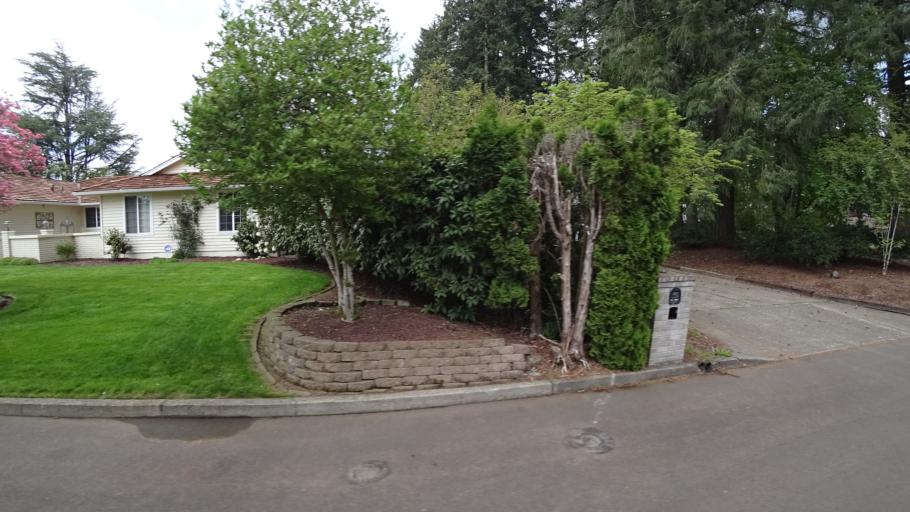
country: US
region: Oregon
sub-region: Washington County
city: Rockcreek
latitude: 45.5553
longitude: -122.8850
